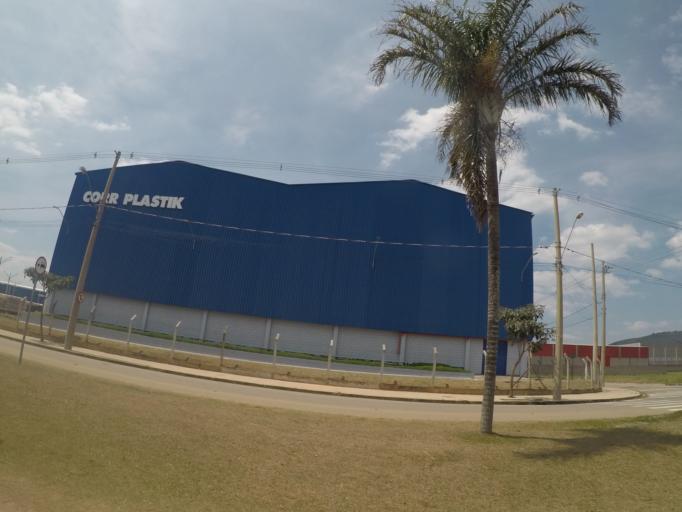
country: BR
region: Sao Paulo
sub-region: Itupeva
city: Itupeva
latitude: -23.2464
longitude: -47.0489
